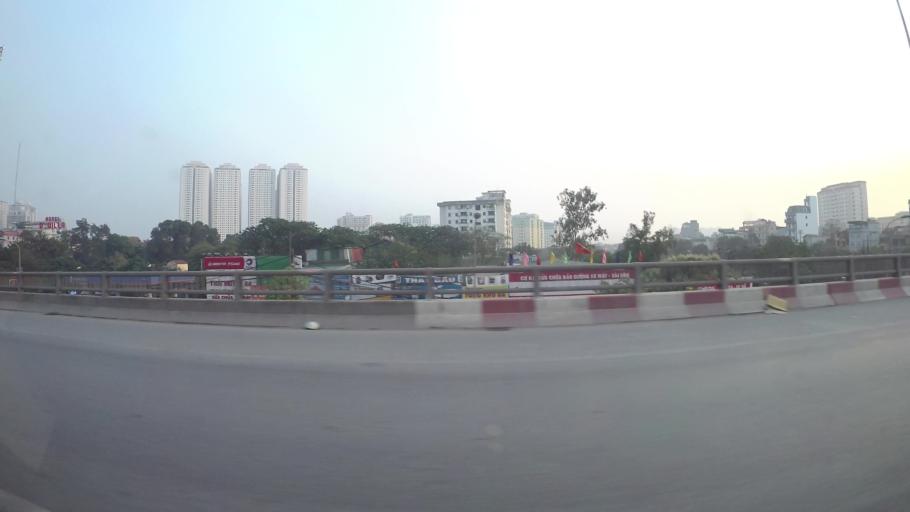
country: VN
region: Ha Noi
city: Van Dien
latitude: 20.9705
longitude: 105.8258
